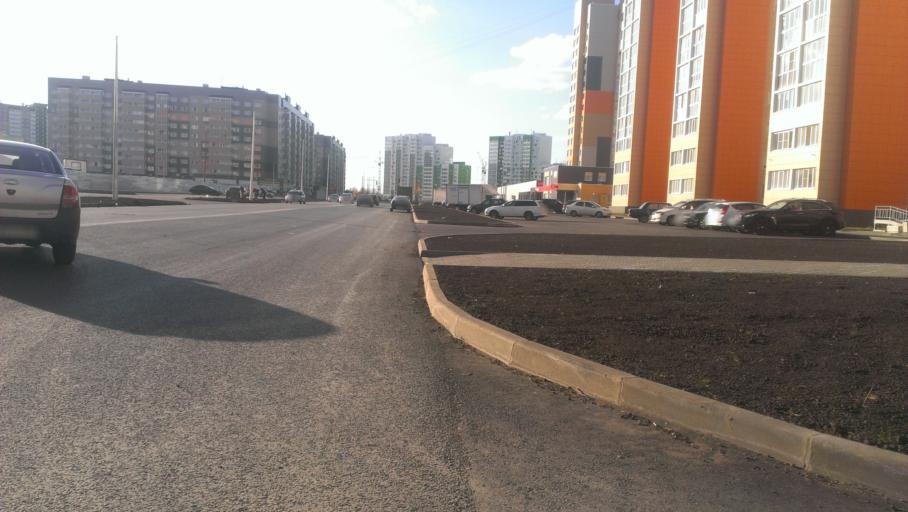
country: RU
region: Altai Krai
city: Novosilikatnyy
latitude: 53.3374
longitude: 83.6568
